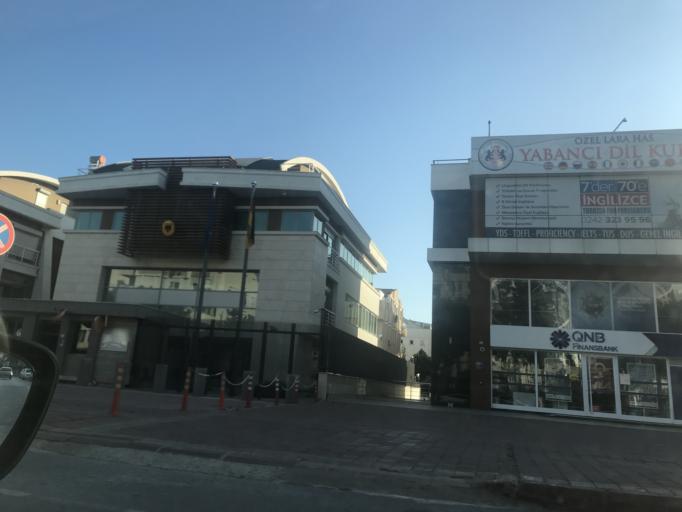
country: TR
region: Antalya
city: Antalya
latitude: 36.8515
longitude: 30.7681
